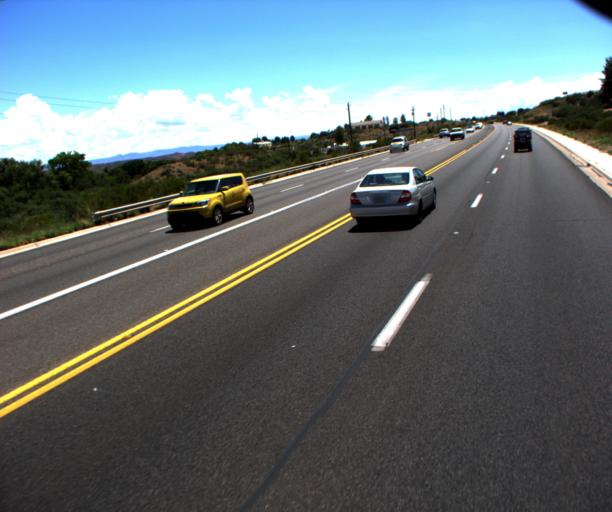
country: US
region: Arizona
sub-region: Yavapai County
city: Verde Village
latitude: 34.7117
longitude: -111.9972
